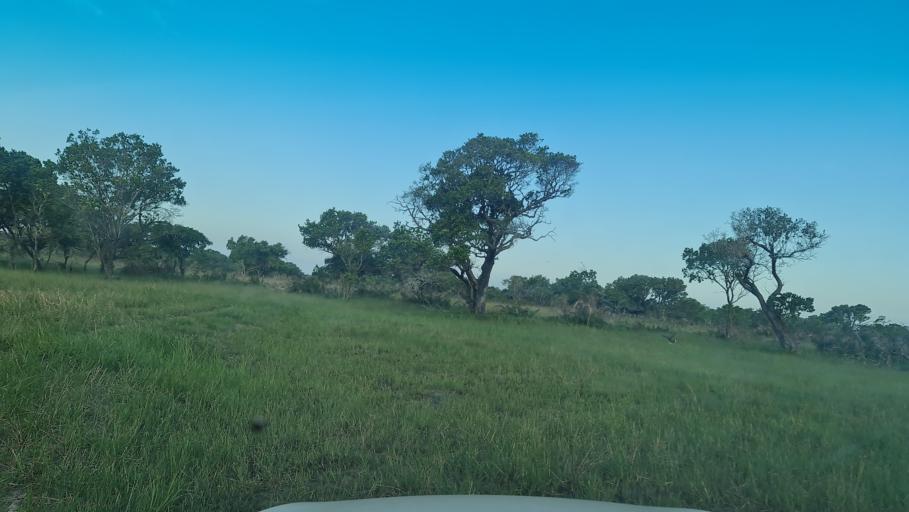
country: MZ
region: Gaza
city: Macia
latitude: -25.2161
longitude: 33.0500
